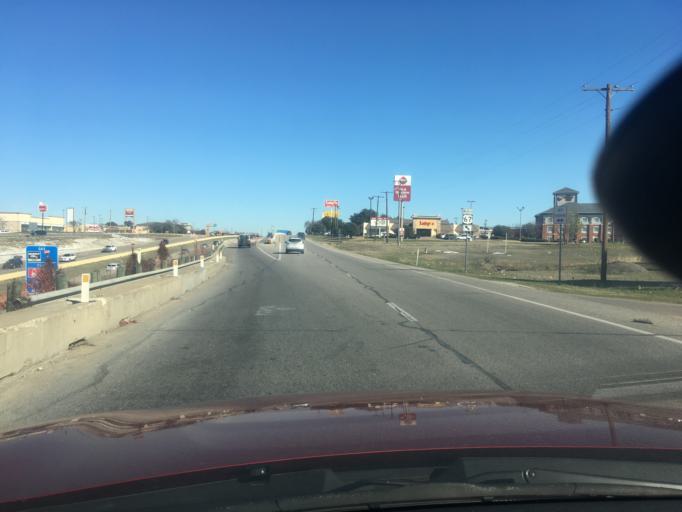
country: US
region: Texas
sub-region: Dallas County
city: Duncanville
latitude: 32.6411
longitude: -96.8906
